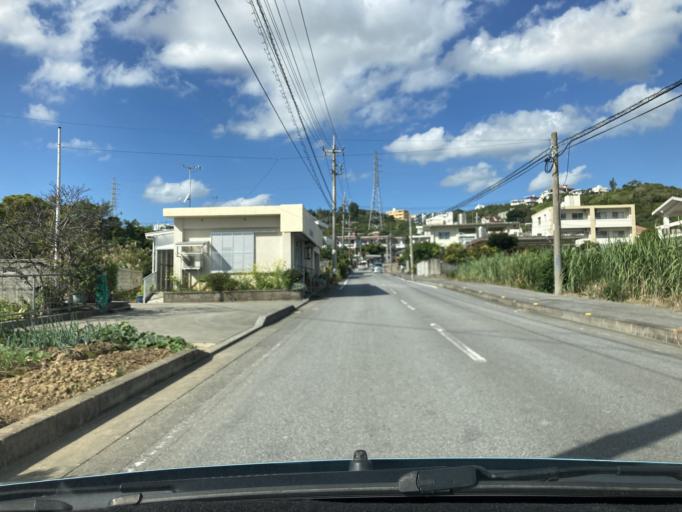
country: JP
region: Okinawa
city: Gushikawa
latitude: 26.3478
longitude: 127.8466
